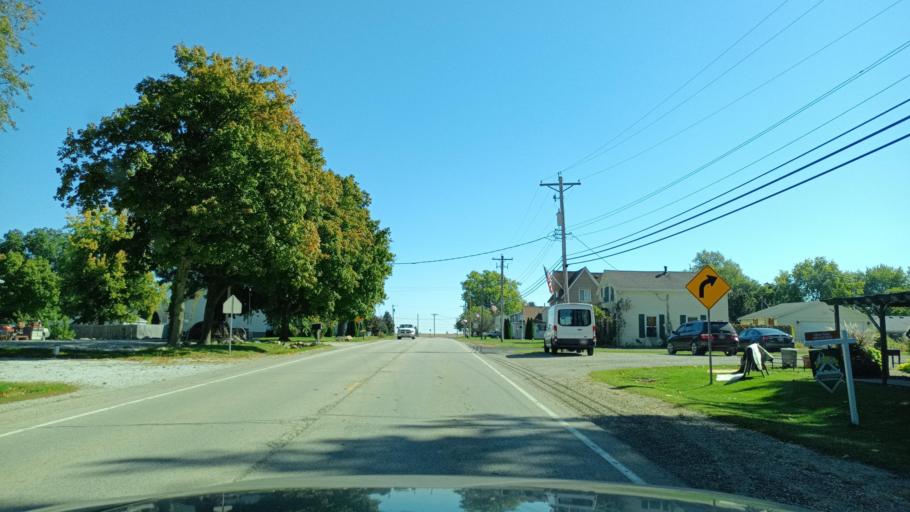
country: US
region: Illinois
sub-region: Peoria County
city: Dunlap
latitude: 40.7898
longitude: -89.7494
